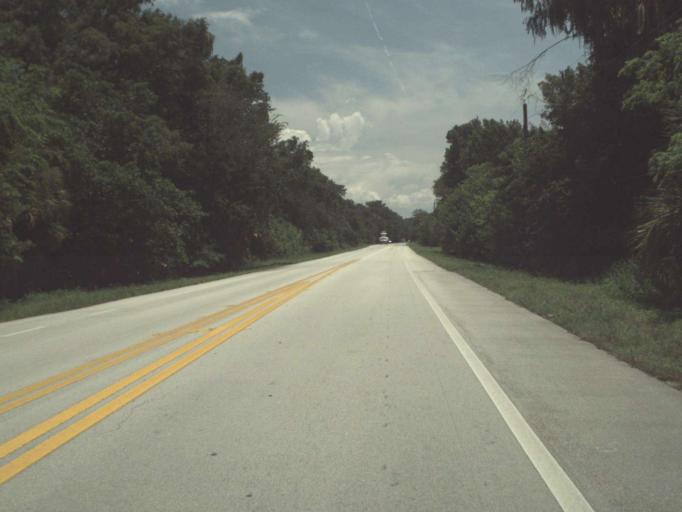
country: US
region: Florida
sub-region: Martin County
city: Indiantown
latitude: 27.0512
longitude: -80.6434
